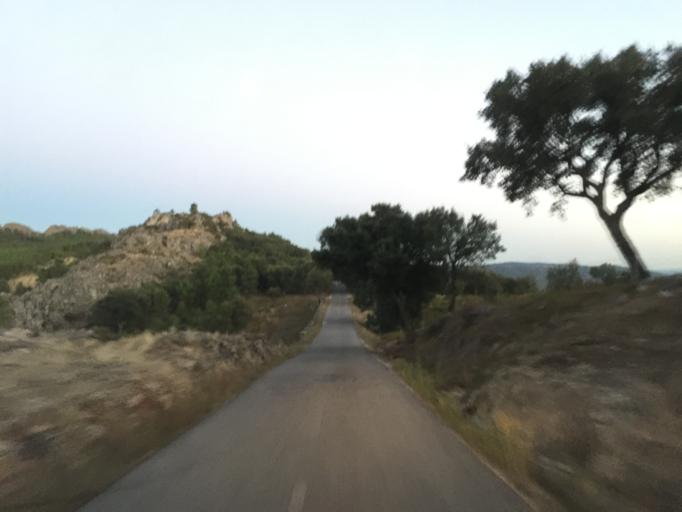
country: PT
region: Portalegre
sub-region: Castelo de Vide
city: Castelo de Vide
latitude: 39.4019
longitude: -7.4529
